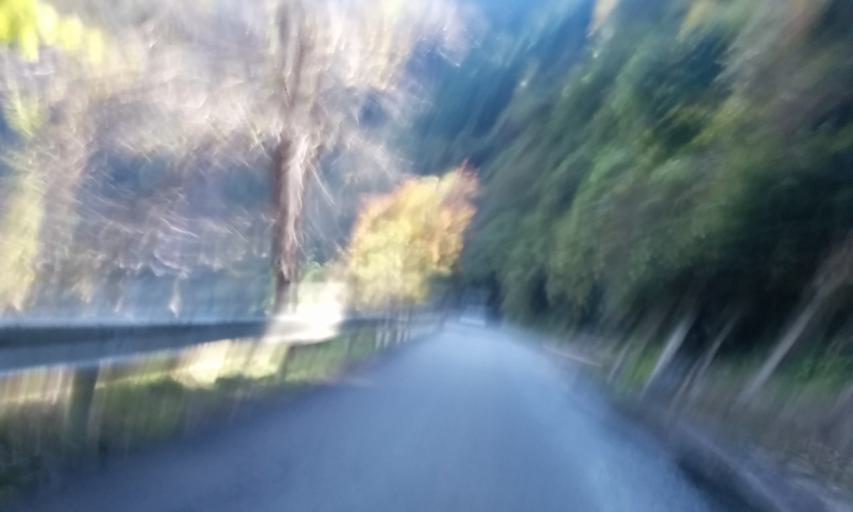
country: JP
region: Kyoto
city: Kameoka
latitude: 35.1290
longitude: 135.5651
